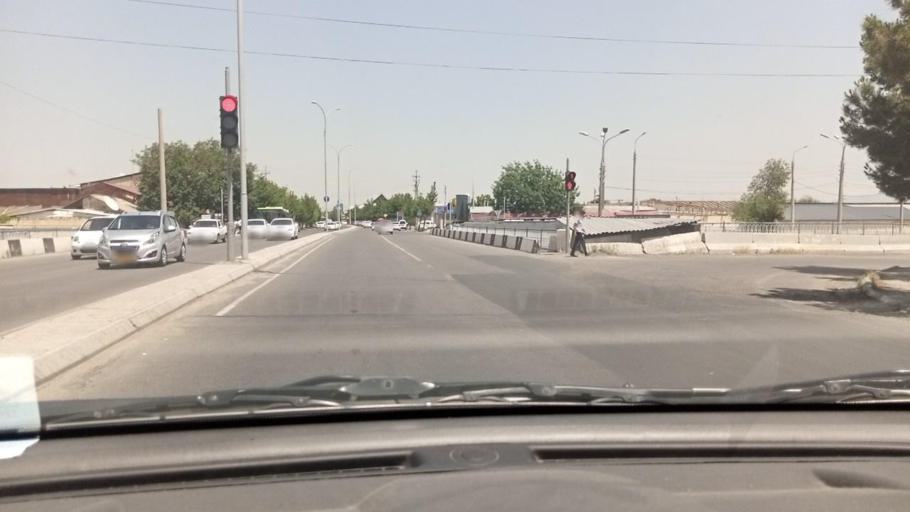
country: UZ
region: Toshkent Shahri
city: Tashkent
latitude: 41.2274
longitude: 69.1810
